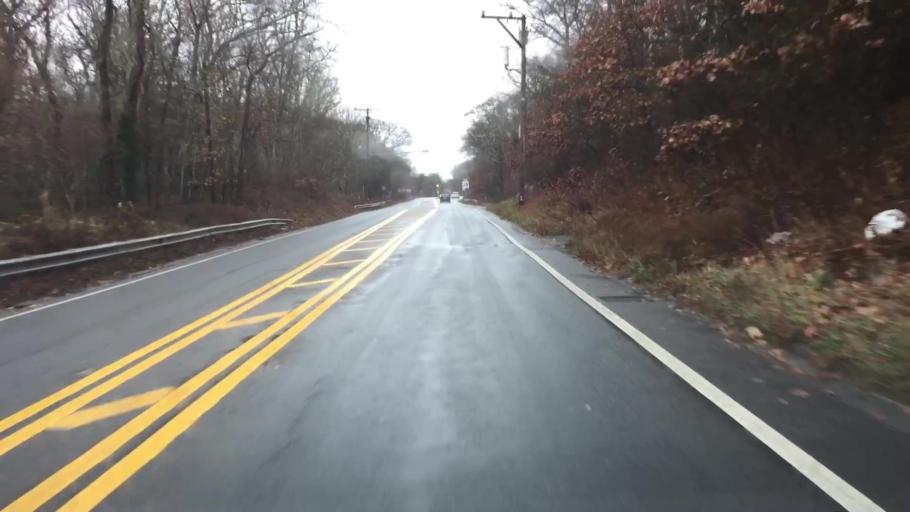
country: US
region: Massachusetts
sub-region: Barnstable County
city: Falmouth
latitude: 41.5772
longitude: -70.6248
